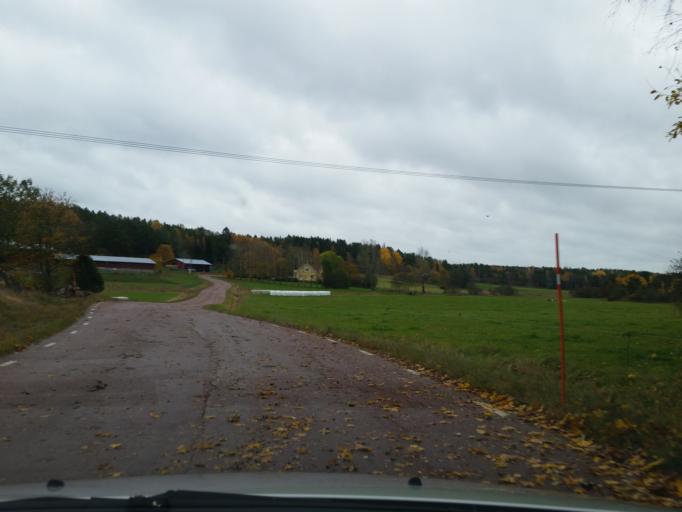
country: AX
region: Alands landsbygd
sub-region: Lumparland
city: Lumparland
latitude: 60.1410
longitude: 20.2676
